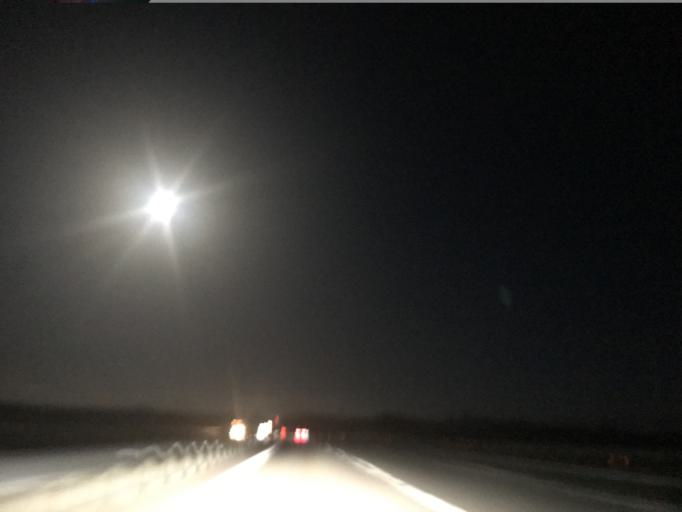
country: TR
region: Nigde
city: Ulukisla
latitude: 37.6402
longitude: 34.3848
